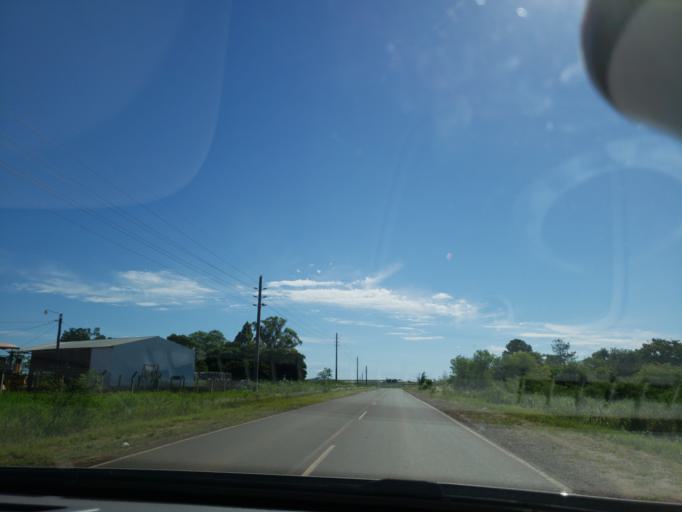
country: AR
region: Misiones
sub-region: Departamento de Capital
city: Posadas
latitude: -27.3872
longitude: -55.9760
